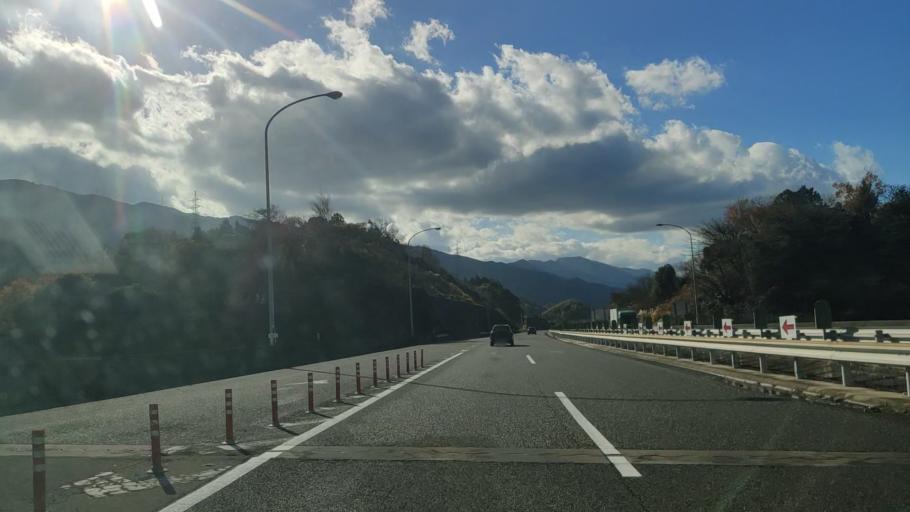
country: JP
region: Ehime
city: Kawanoecho
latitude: 33.9831
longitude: 133.5860
